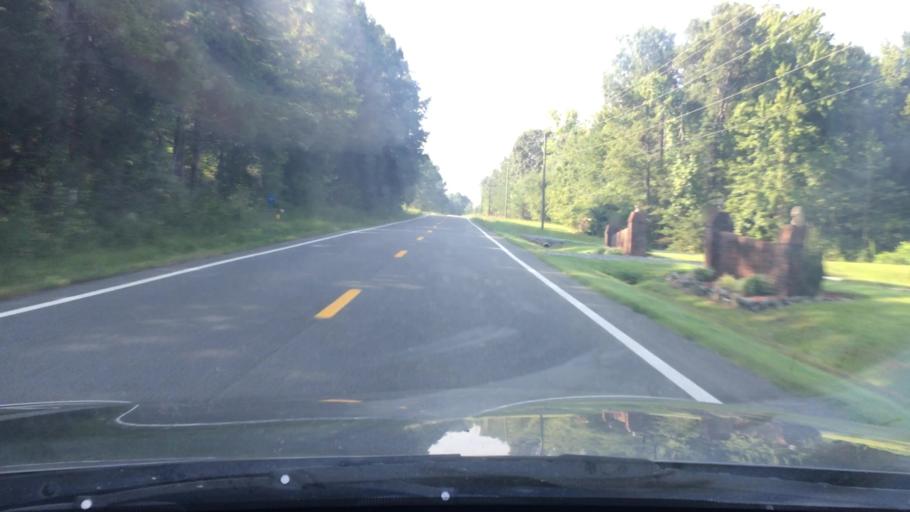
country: US
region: North Carolina
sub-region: Alamance County
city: Green Level
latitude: 36.2198
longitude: -79.3222
